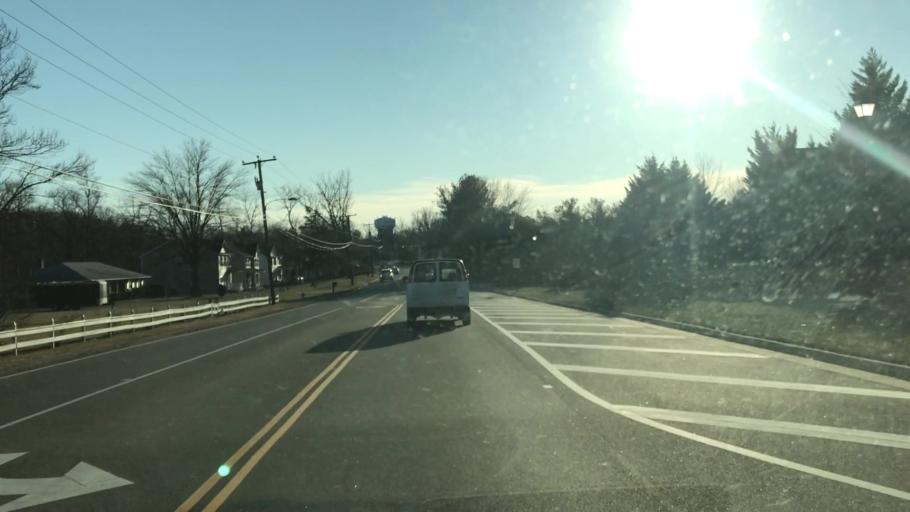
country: US
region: Virginia
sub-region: City of Fredericksburg
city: Fredericksburg
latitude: 38.2843
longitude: -77.4798
